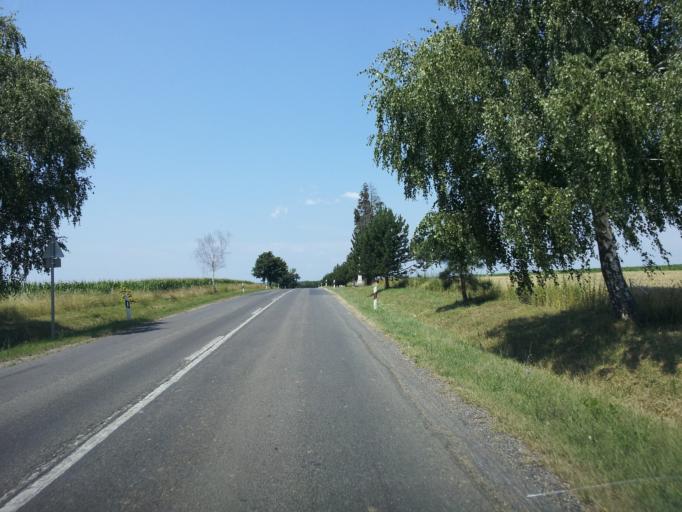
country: HU
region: Zala
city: Zalaegerszeg
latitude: 46.8739
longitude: 16.7666
